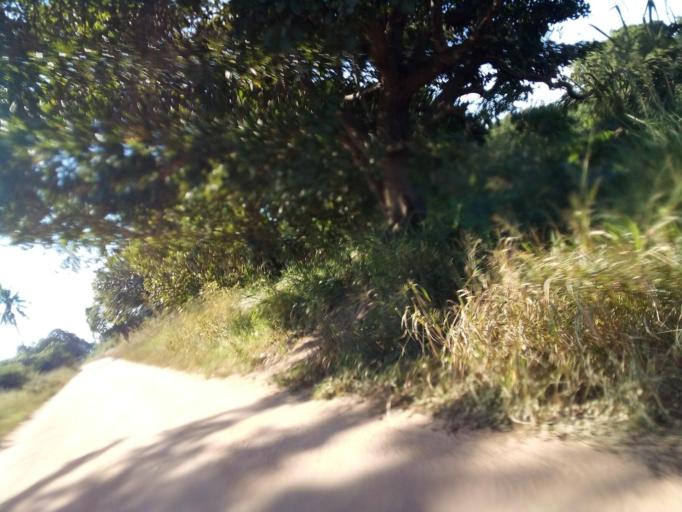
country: MZ
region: Zambezia
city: Quelimane
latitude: -17.5392
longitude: 36.6243
